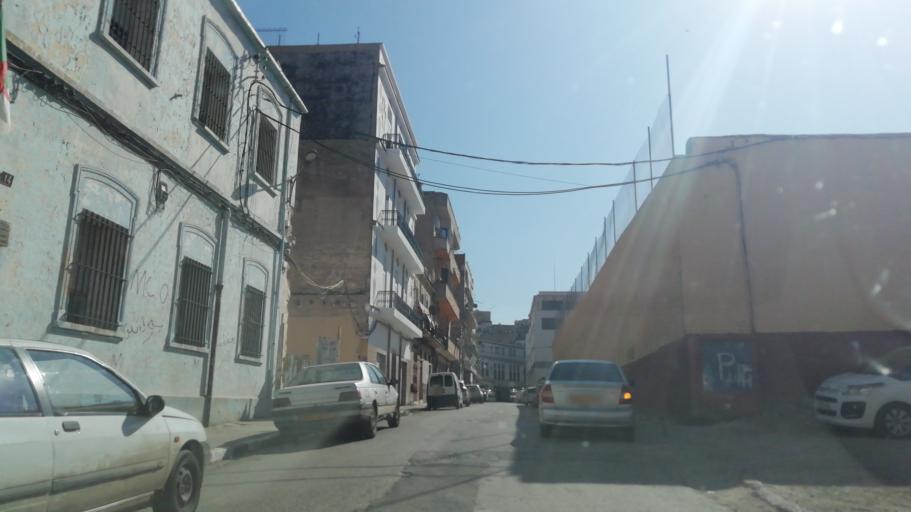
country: DZ
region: Oran
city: Oran
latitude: 35.7054
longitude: -0.6437
